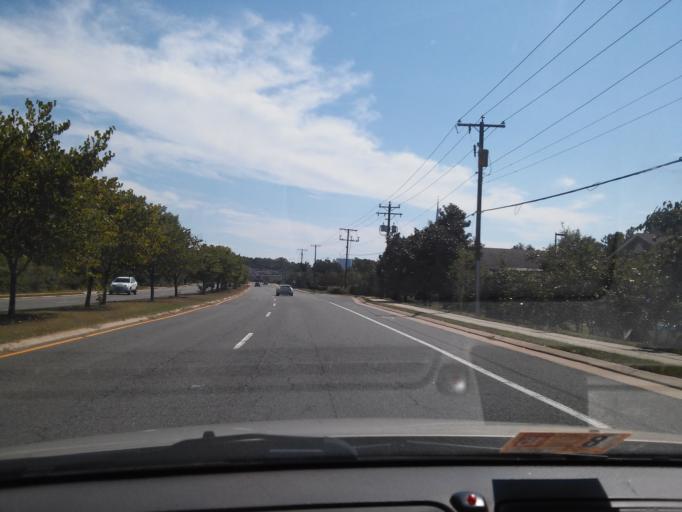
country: US
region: Virginia
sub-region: Chesterfield County
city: Bon Air
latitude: 37.5104
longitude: -77.5868
